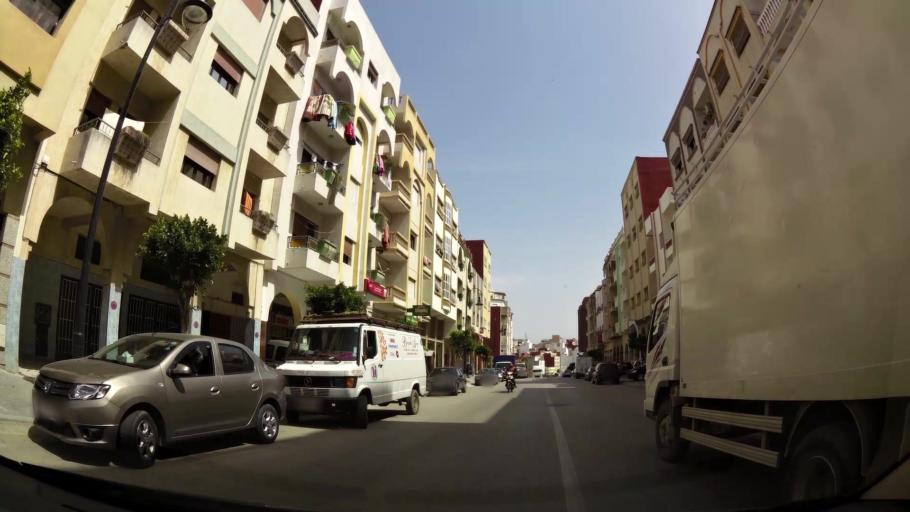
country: MA
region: Tanger-Tetouan
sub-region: Tanger-Assilah
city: Tangier
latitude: 35.7557
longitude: -5.8345
